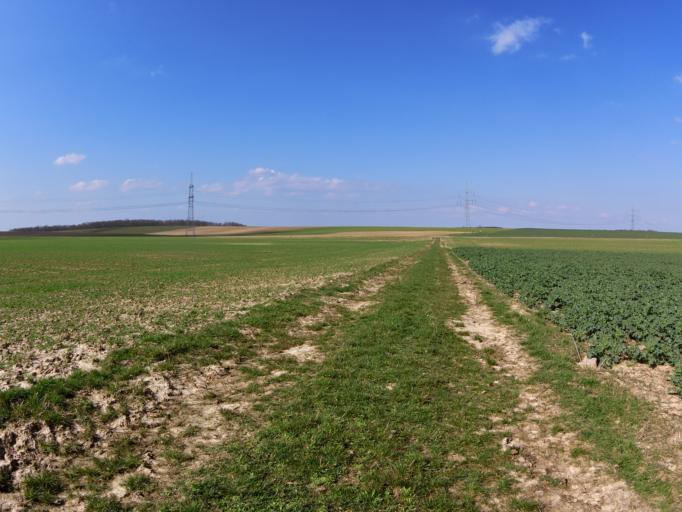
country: DE
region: Bavaria
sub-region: Regierungsbezirk Unterfranken
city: Biebelried
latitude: 49.7961
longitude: 10.0694
